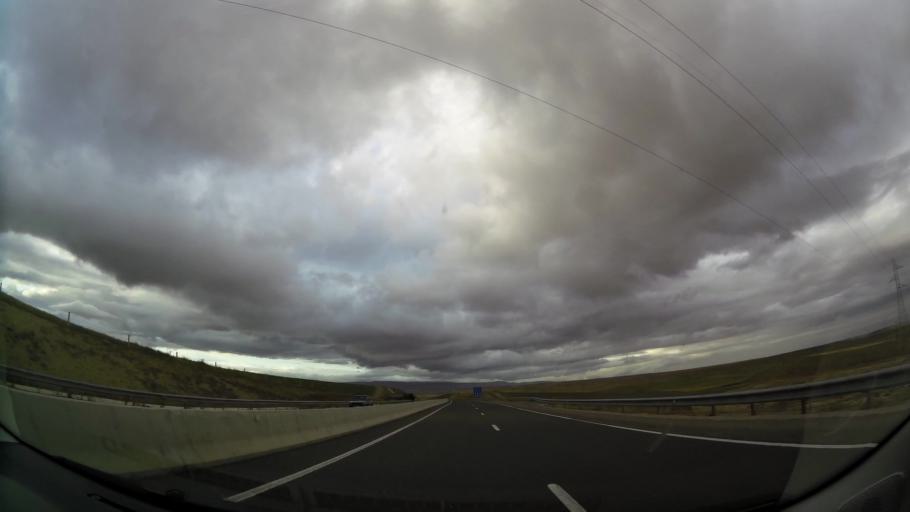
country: MA
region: Taza-Al Hoceima-Taounate
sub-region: Taza
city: Taza
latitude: 34.2783
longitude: -3.7918
